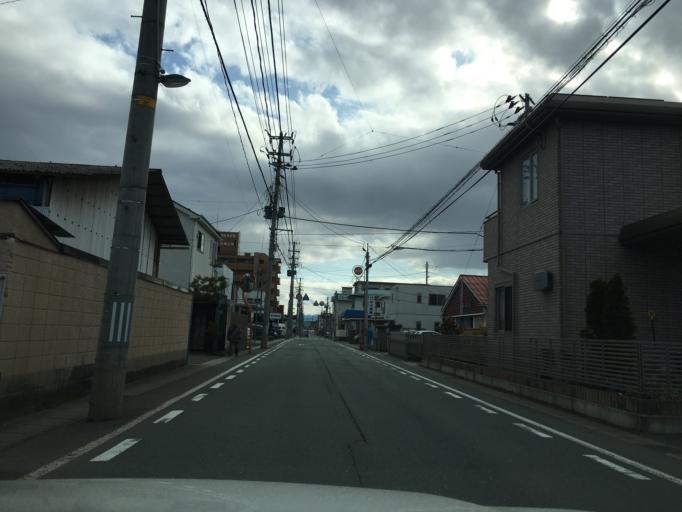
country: JP
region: Yamagata
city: Yamagata-shi
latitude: 38.2566
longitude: 140.3241
